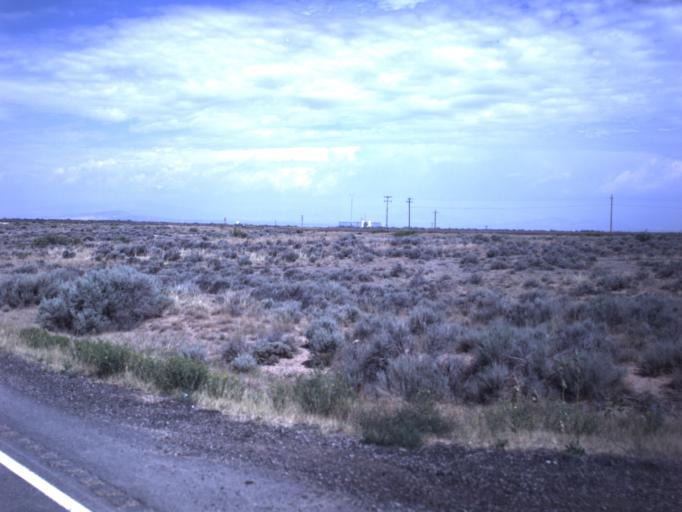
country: US
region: Utah
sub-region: Uintah County
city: Naples
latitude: 40.2017
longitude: -109.3510
